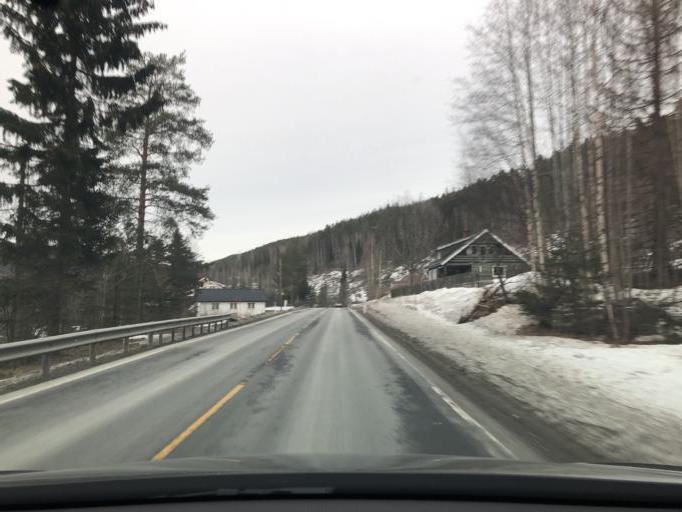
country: NO
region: Buskerud
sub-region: Ringerike
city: Honefoss
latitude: 60.4284
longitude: 10.0977
